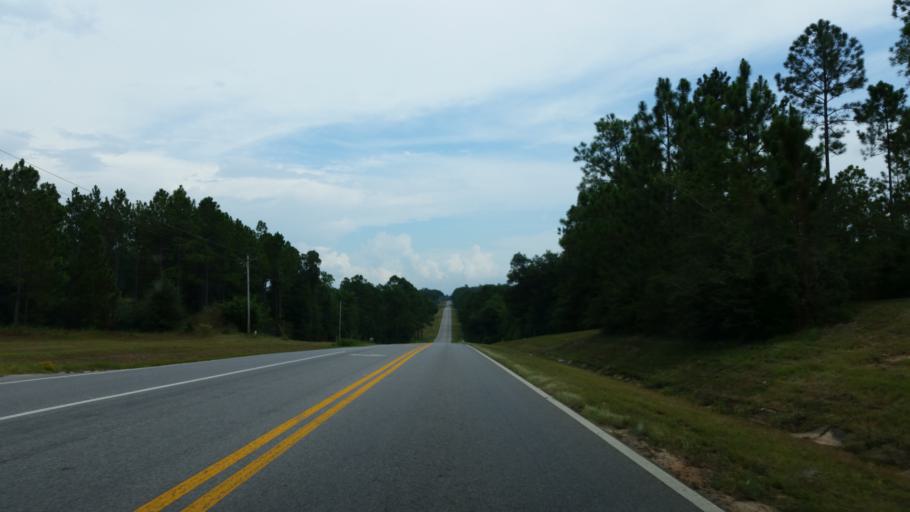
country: US
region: Florida
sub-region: Santa Rosa County
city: Wallace
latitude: 30.6706
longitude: -87.2165
